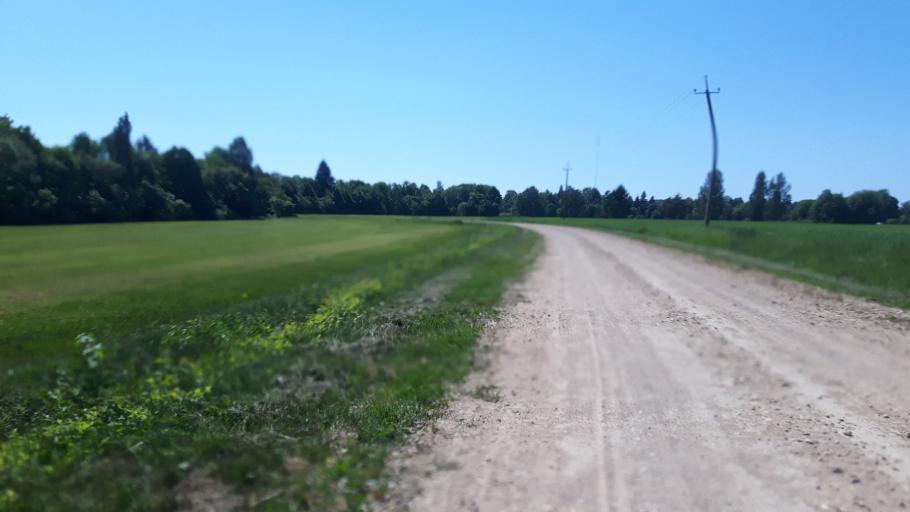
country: EE
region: Paernumaa
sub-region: Tootsi vald
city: Tootsi
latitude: 58.4975
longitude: 24.9014
